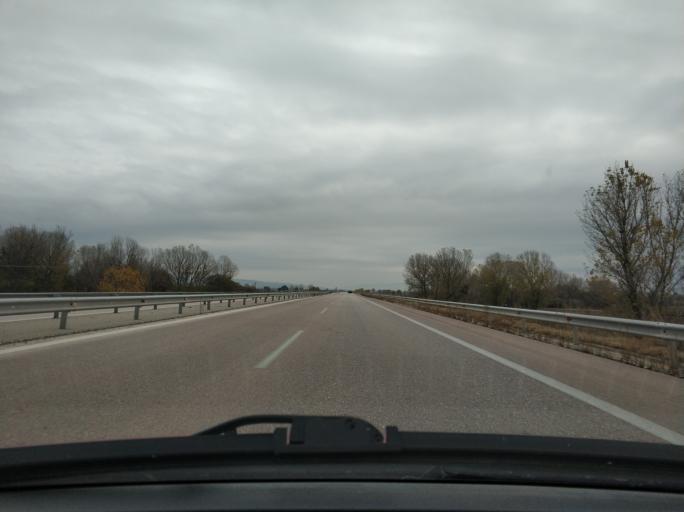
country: GR
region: Central Macedonia
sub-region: Nomos Thessalonikis
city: Kavallari
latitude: 40.7296
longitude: 23.0608
